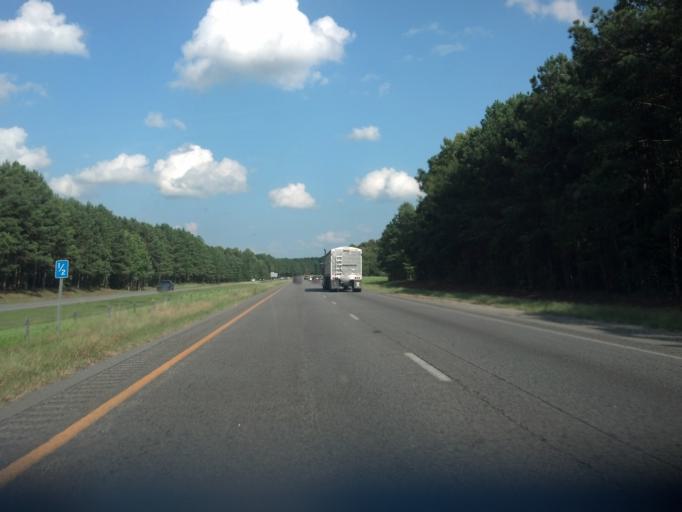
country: US
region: North Carolina
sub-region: Nash County
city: Rocky Mount
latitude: 35.9355
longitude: -77.7297
